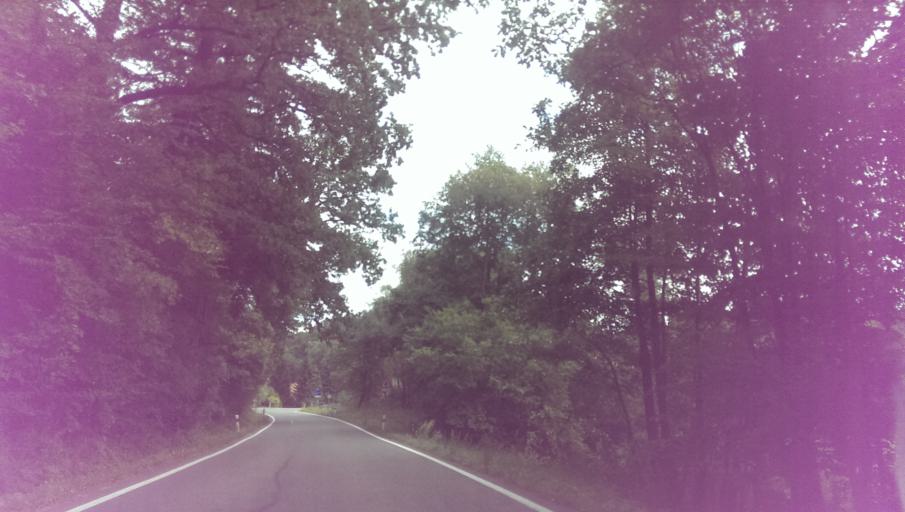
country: CZ
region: South Moravian
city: Velka nad Velickou
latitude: 48.8826
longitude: 17.5845
